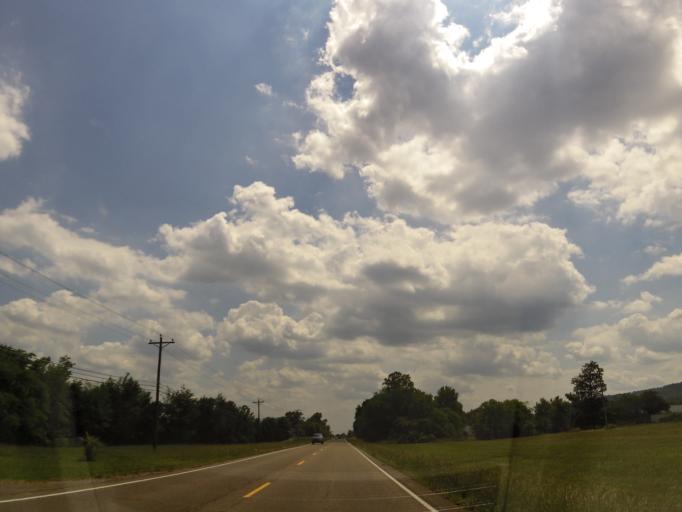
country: US
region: Tennessee
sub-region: Bledsoe County
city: Pikeville
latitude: 35.5604
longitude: -85.2481
